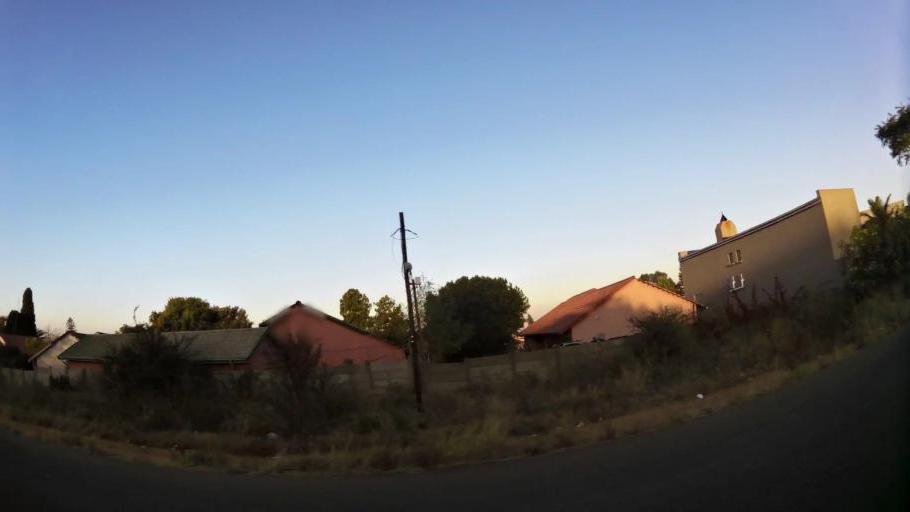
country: ZA
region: North-West
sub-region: Bojanala Platinum District Municipality
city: Rustenburg
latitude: -25.6368
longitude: 27.2010
